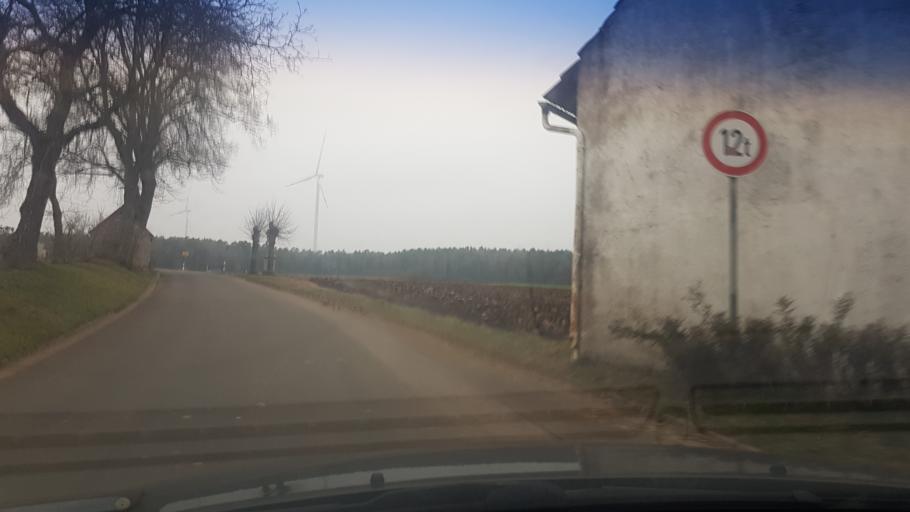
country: DE
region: Bavaria
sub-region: Upper Franconia
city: Kasendorf
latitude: 50.0360
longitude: 11.2925
